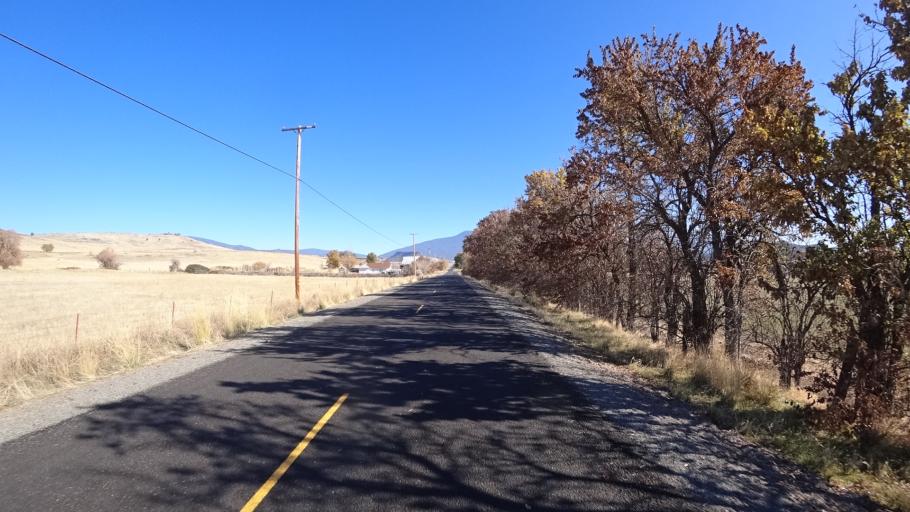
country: US
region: California
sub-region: Siskiyou County
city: Montague
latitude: 41.7263
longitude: -122.3924
